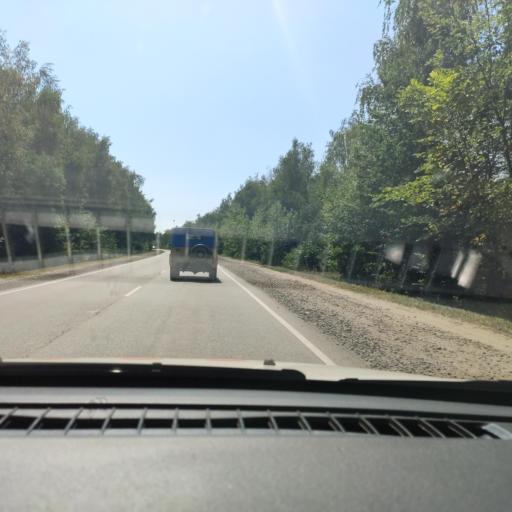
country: RU
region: Voronezj
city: Imeni Pervogo Maya
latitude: 50.7437
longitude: 39.3871
